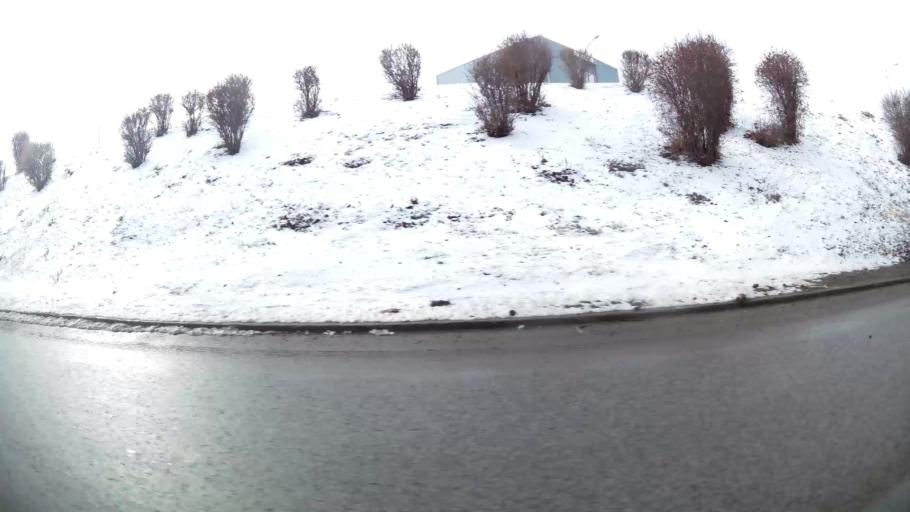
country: BG
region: Sofia-Capital
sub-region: Stolichna Obshtina
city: Sofia
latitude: 42.7058
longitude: 23.4037
